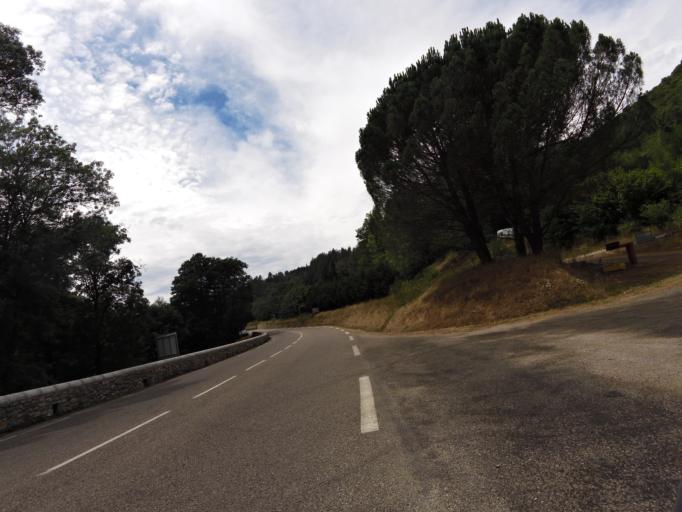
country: FR
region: Languedoc-Roussillon
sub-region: Departement du Gard
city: Le Vigan
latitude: 44.0015
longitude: 3.6564
